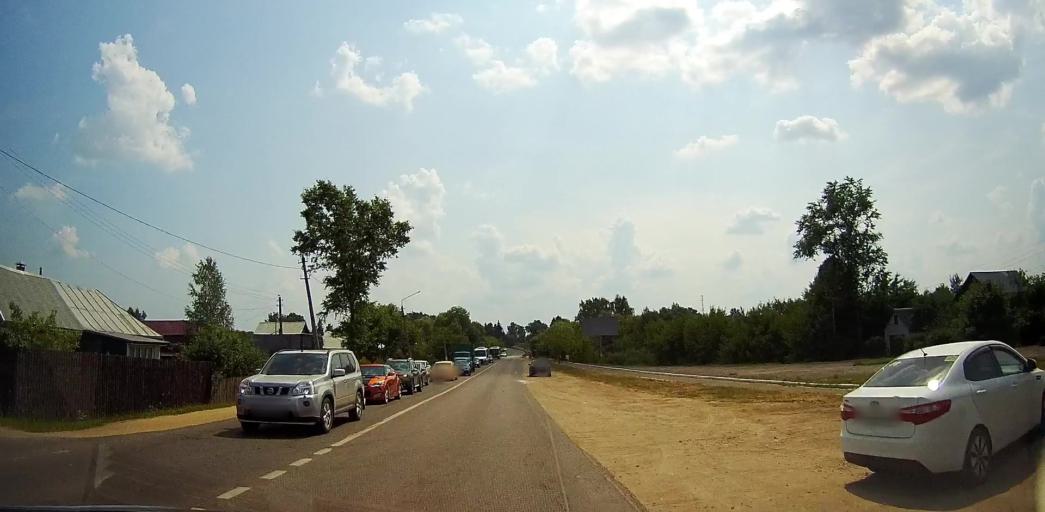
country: RU
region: Moskovskaya
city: Malino
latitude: 55.1112
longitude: 38.1776
